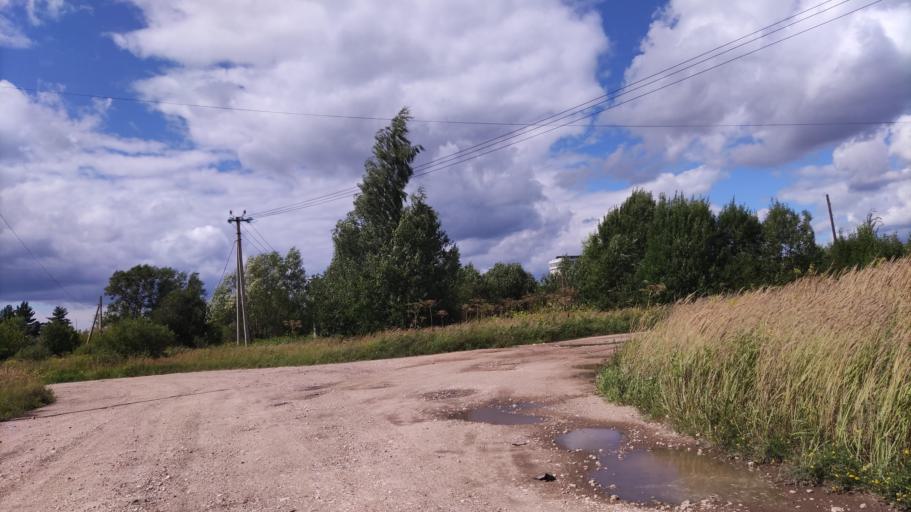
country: RU
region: Tverskaya
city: Rzhev
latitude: 56.2398
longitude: 34.3073
